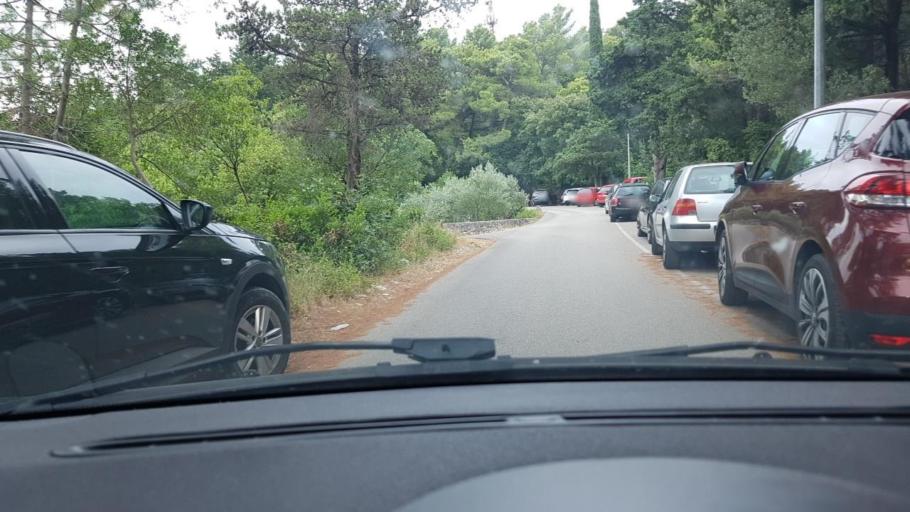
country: HR
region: Dubrovacko-Neretvanska
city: Korcula
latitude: 42.9609
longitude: 17.1297
